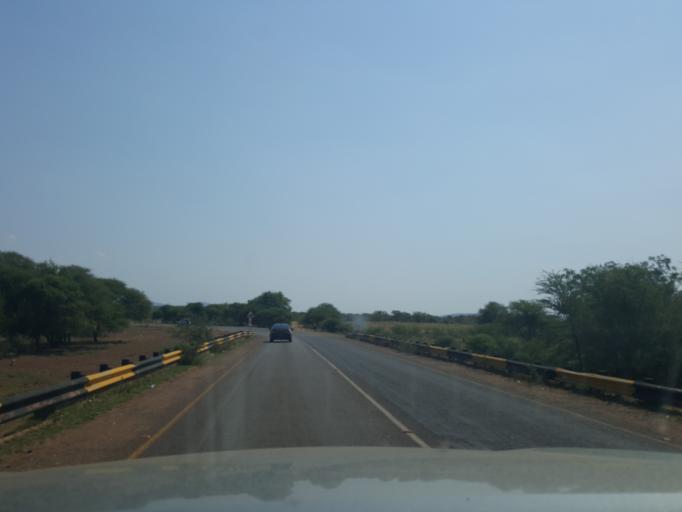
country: BW
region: South East
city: Ramotswa
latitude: -24.8506
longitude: 25.8292
